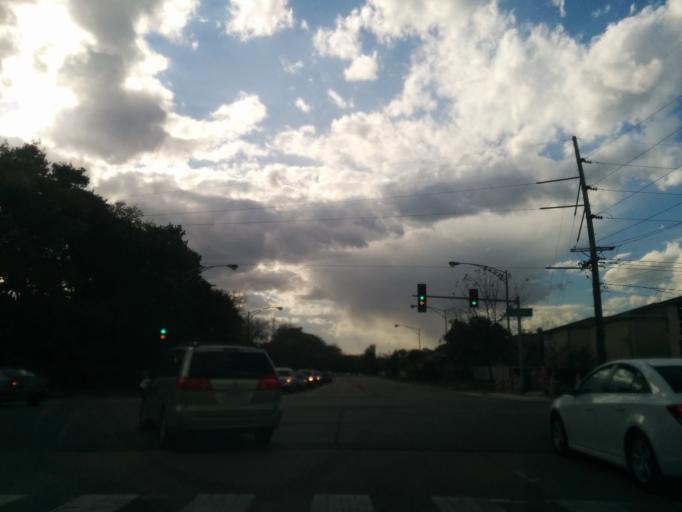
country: US
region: Illinois
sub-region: Cook County
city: Norridge
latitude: 41.9594
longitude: -87.8364
